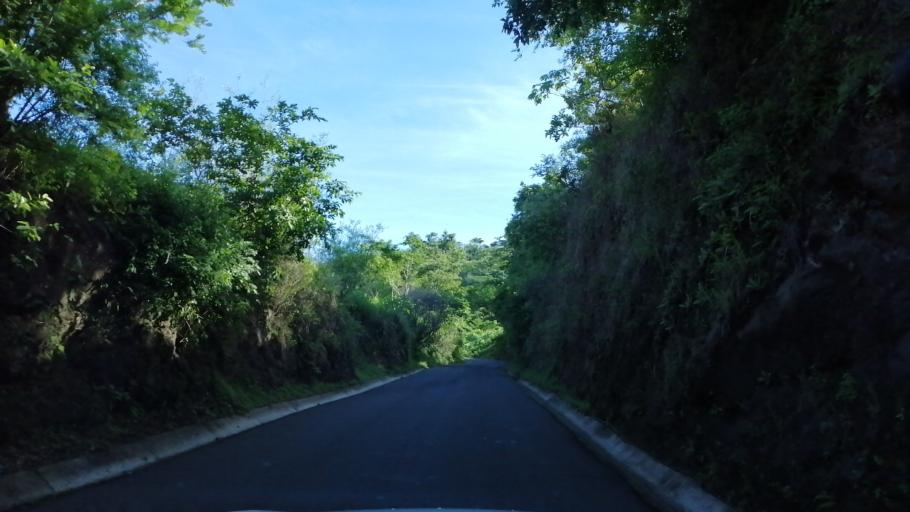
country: SV
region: Morazan
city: Corinto
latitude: 13.7963
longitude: -88.0074
